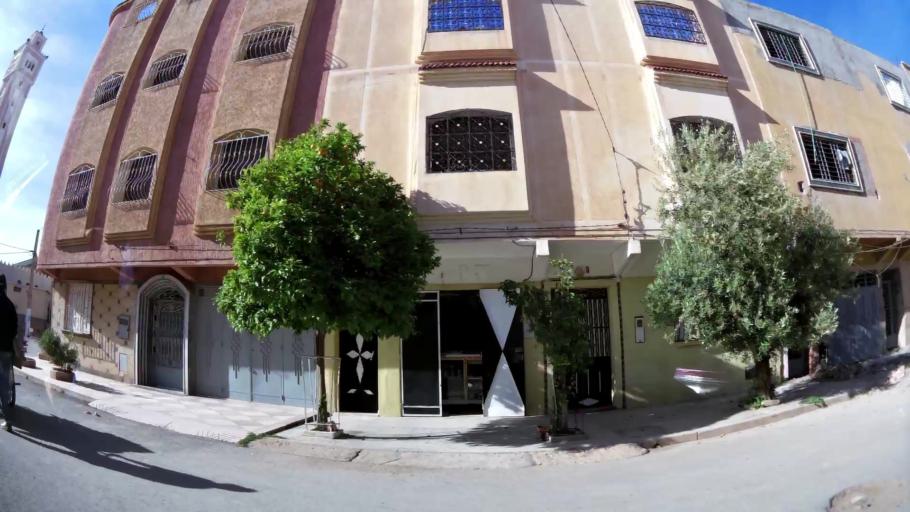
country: MA
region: Oriental
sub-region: Oujda-Angad
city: Oujda
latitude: 34.6719
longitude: -1.8955
